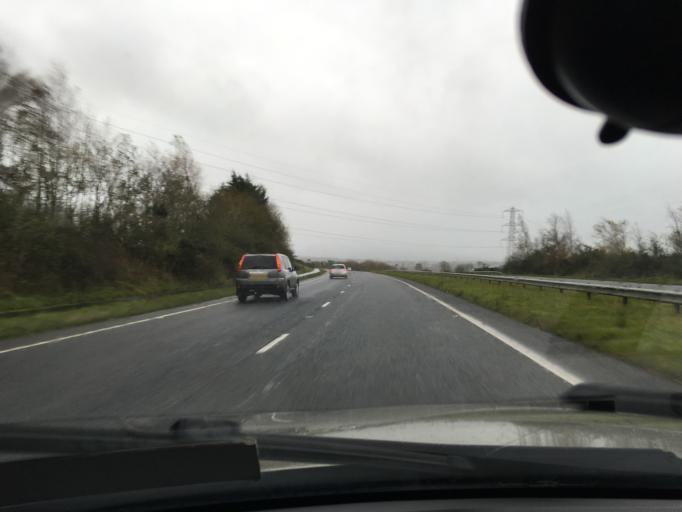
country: GB
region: Northern Ireland
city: Carnmoney
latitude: 54.7139
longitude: -5.9681
